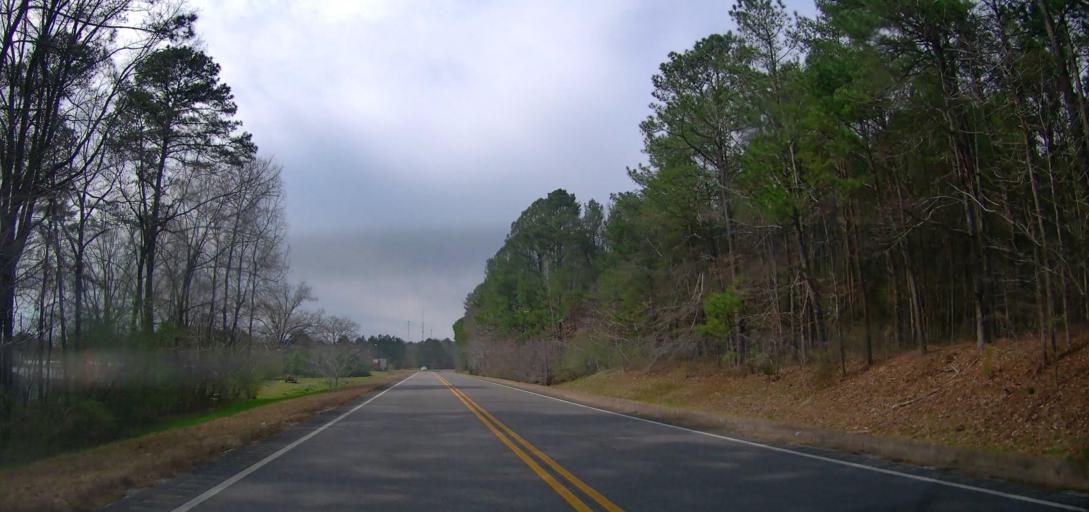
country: US
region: Alabama
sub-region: Walker County
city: Carbon Hill
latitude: 33.9007
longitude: -87.5445
